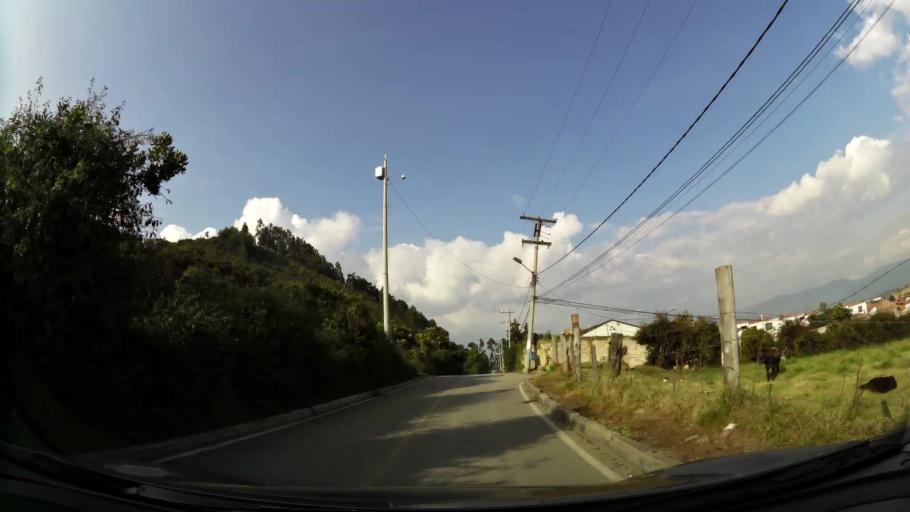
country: CO
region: Cundinamarca
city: Cota
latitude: 4.8080
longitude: -74.1109
